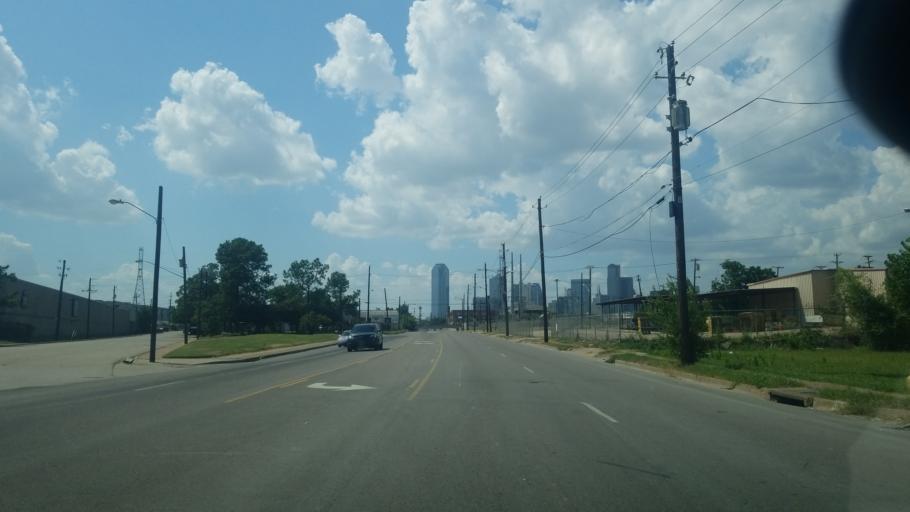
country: US
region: Texas
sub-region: Dallas County
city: Dallas
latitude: 32.7600
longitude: -96.7834
